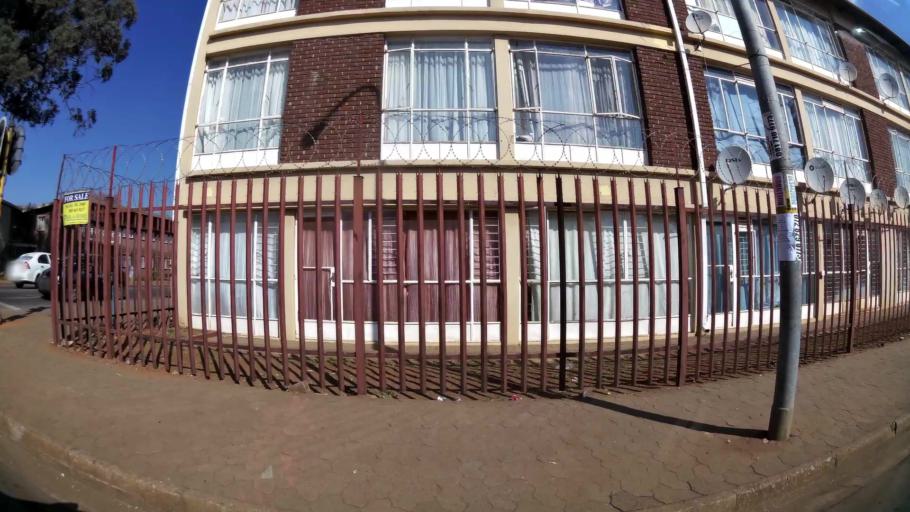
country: ZA
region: Gauteng
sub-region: City of Johannesburg Metropolitan Municipality
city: Modderfontein
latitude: -26.1062
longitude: 28.2374
